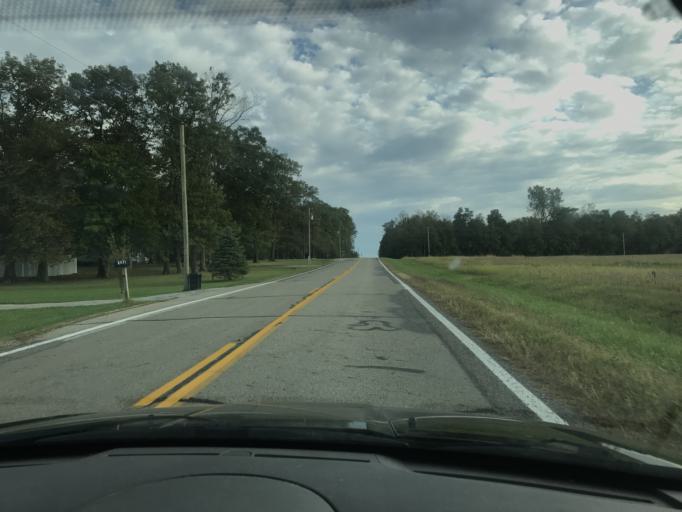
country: US
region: Ohio
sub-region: Champaign County
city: North Lewisburg
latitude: 40.2338
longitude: -83.6441
